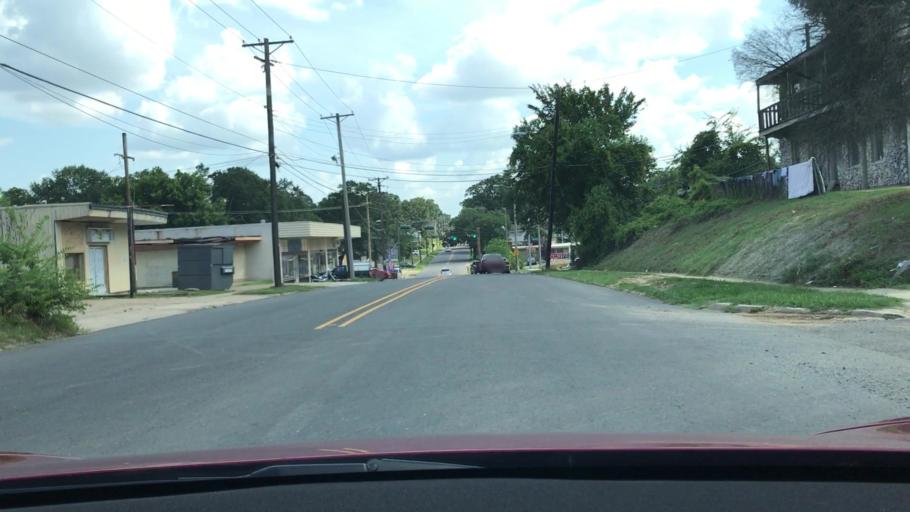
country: US
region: Louisiana
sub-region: Bossier Parish
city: Bossier City
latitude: 32.4936
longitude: -93.7333
